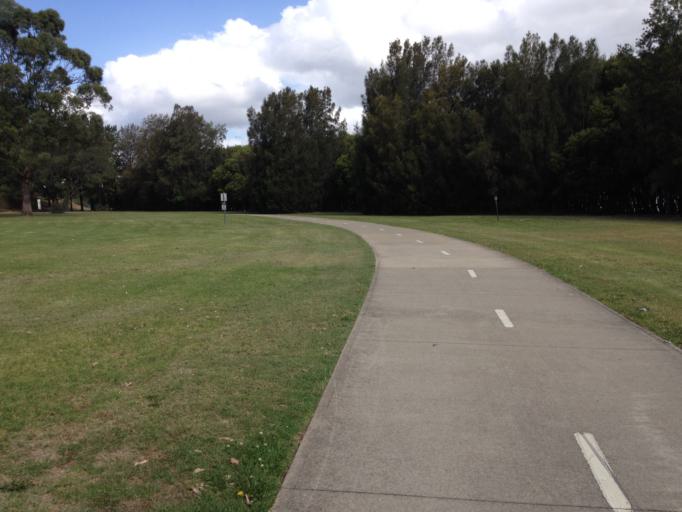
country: AU
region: New South Wales
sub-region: Parramatta
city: Ermington
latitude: -33.8222
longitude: 151.0498
